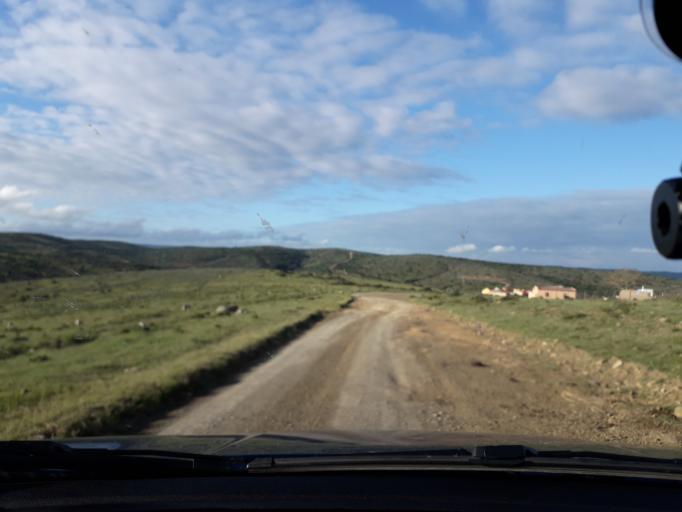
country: ZA
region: Eastern Cape
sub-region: Buffalo City Metropolitan Municipality
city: Bhisho
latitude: -33.1284
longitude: 27.4407
